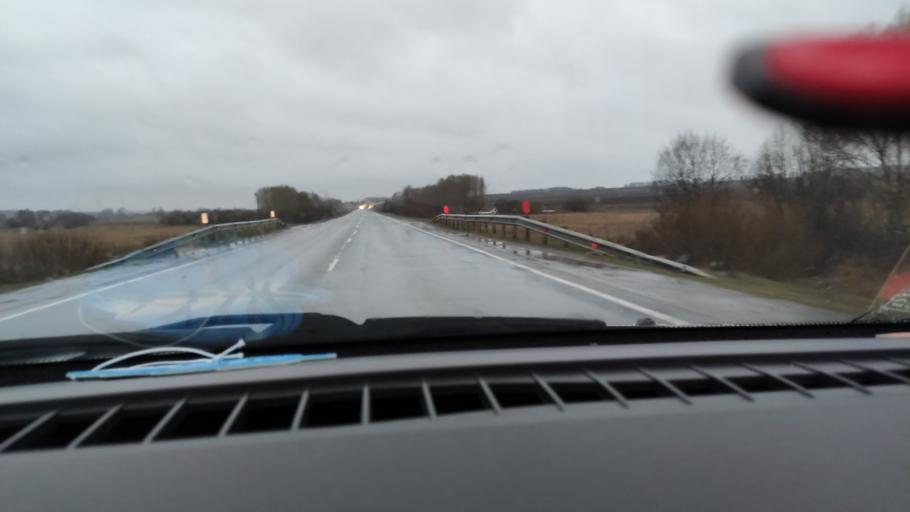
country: RU
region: Tatarstan
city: Mendeleyevsk
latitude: 55.9666
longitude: 52.3164
